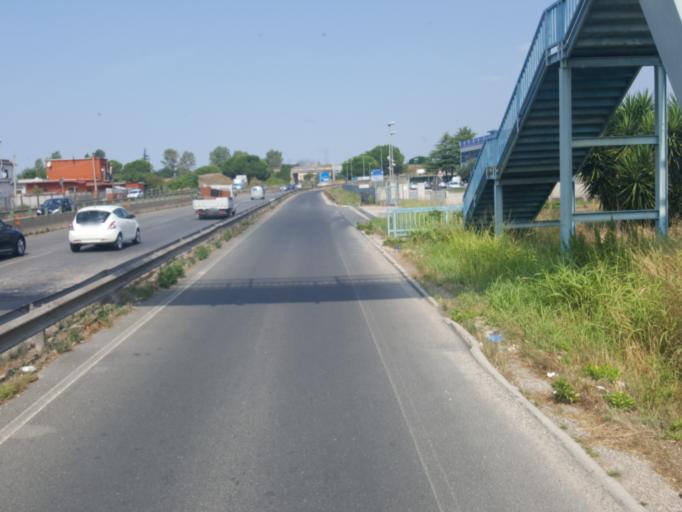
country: IT
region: Latium
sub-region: Provincia di Latina
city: Aprilia
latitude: 41.5770
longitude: 12.6553
